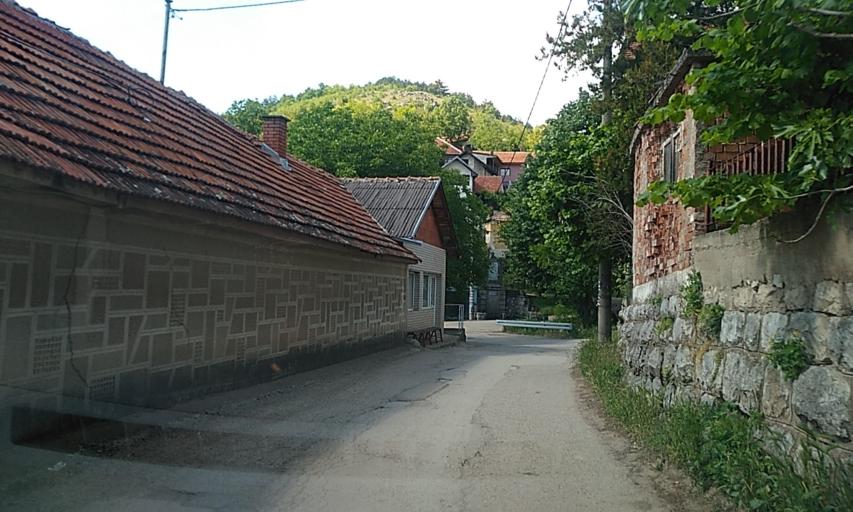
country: RS
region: Central Serbia
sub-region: Nisavski Okrug
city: Niska Banja
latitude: 43.3666
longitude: 22.0009
